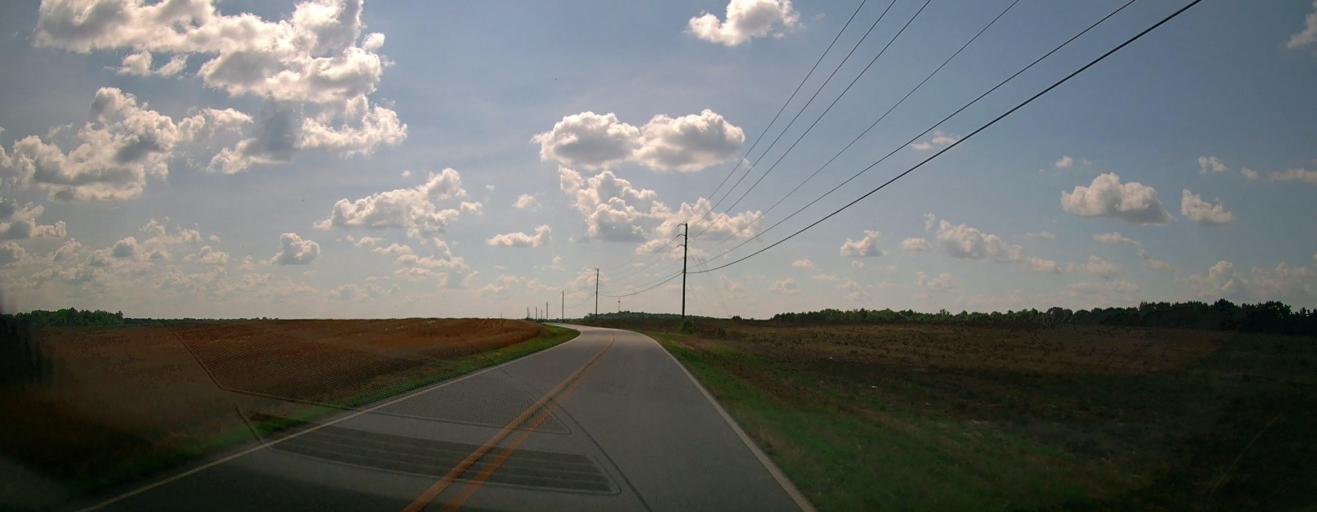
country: US
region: Georgia
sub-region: Henry County
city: Locust Grove
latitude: 33.2246
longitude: -84.1073
